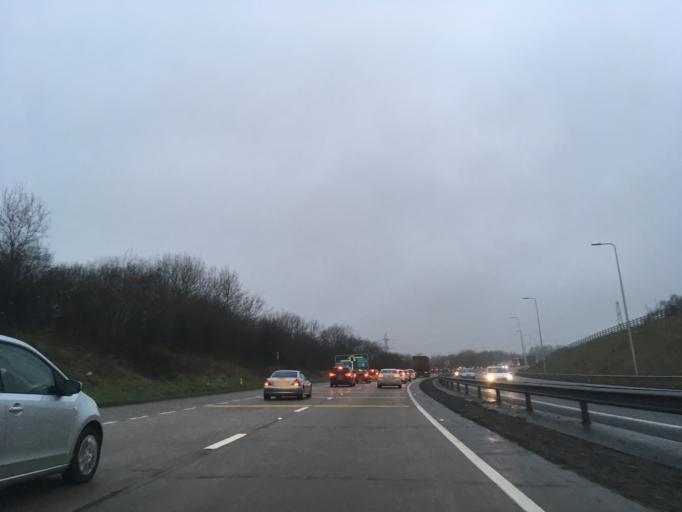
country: GB
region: Wales
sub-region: Cardiff
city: Pentyrch
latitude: 51.5025
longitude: -3.3056
